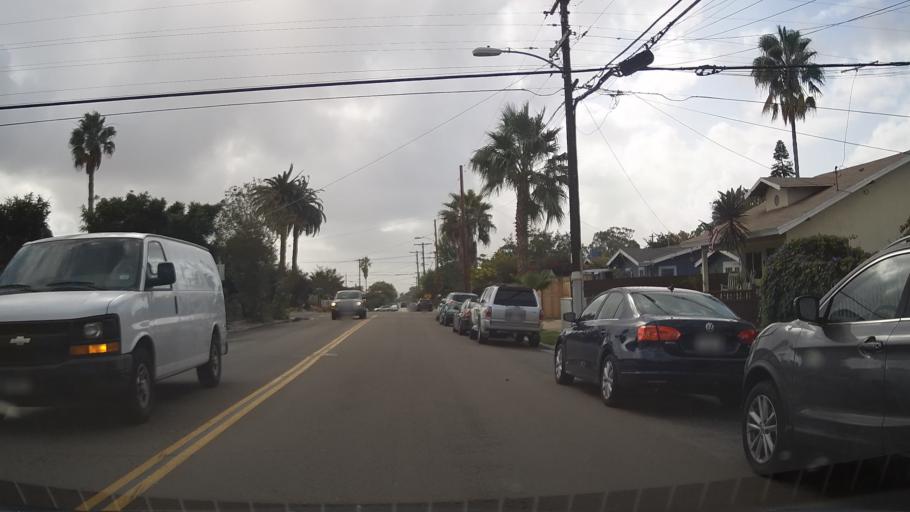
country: US
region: California
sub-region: San Diego County
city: San Diego
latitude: 32.7283
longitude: -117.1275
